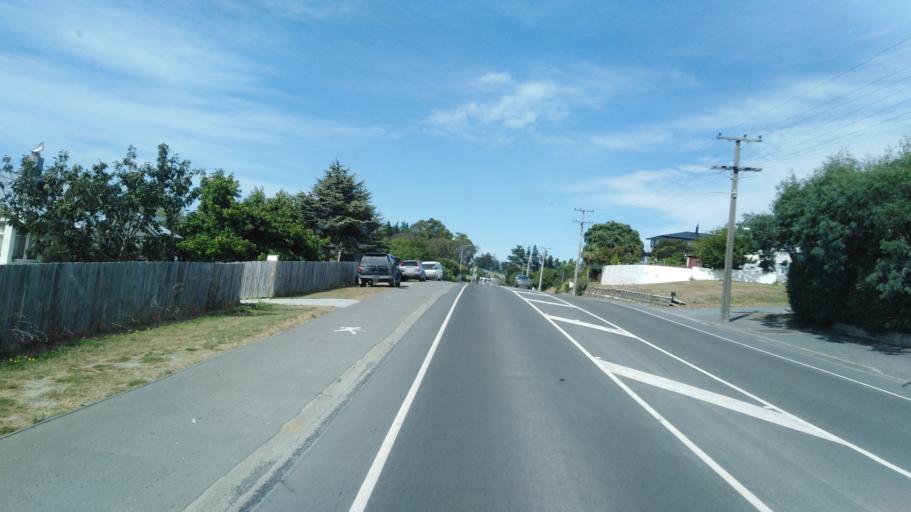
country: NZ
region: Canterbury
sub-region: Kaikoura District
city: Kaikoura
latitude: -42.4076
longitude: 173.6790
